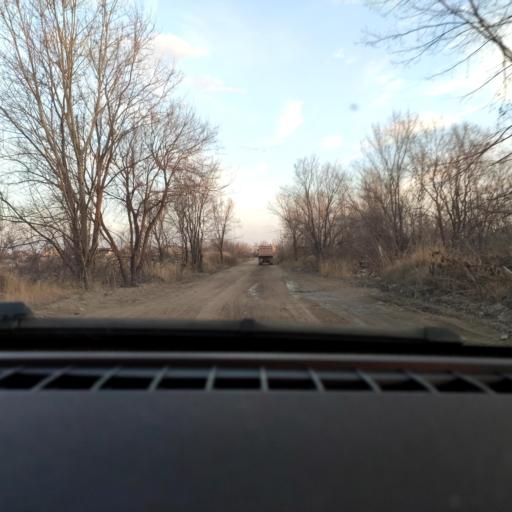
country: RU
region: Voronezj
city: Maslovka
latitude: 51.6113
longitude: 39.2670
